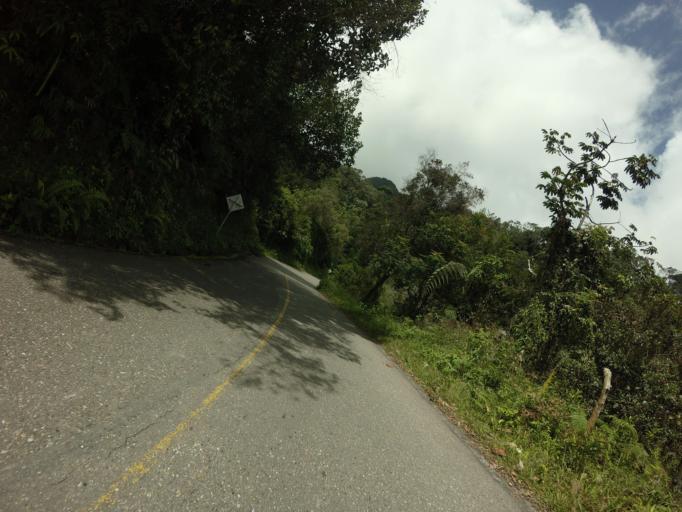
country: CO
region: Caldas
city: Manzanares
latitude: 5.2747
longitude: -75.1185
